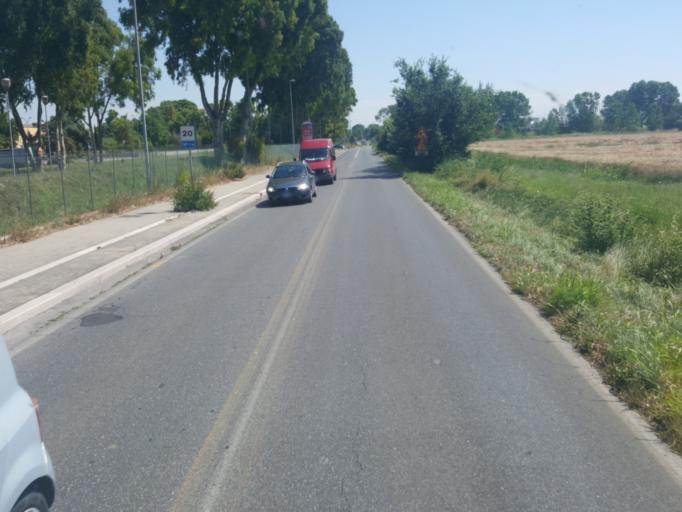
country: IT
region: Latium
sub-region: Citta metropolitana di Roma Capitale
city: Npp 23 (Parco Leonardo)
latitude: 41.8014
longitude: 12.3094
